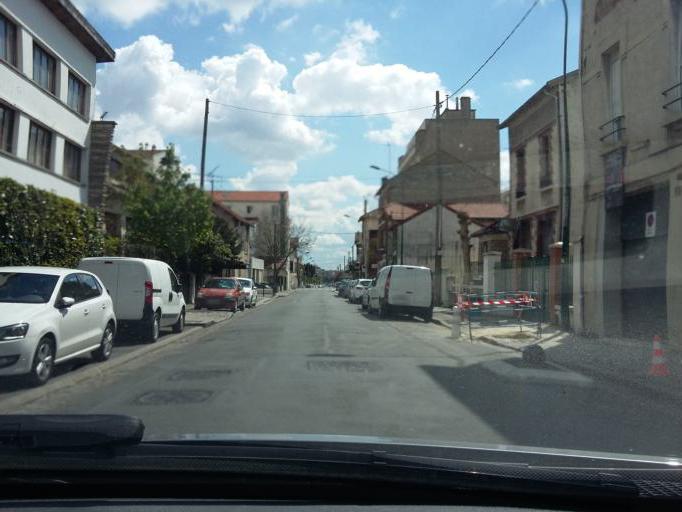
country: FR
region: Ile-de-France
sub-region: Departement du Val-d'Oise
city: Saint-Gratien
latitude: 48.9641
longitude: 2.2964
